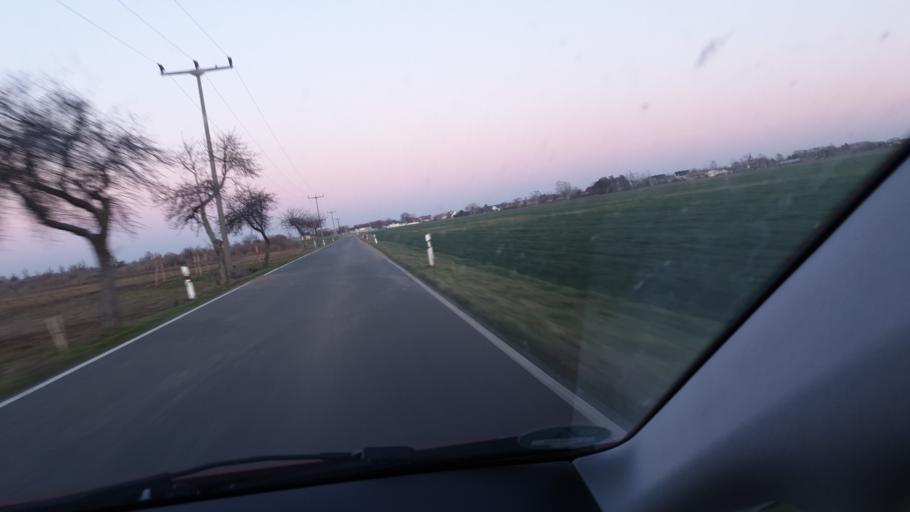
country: DE
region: Saxony
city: Mockrehna
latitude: 51.4757
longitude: 12.8386
